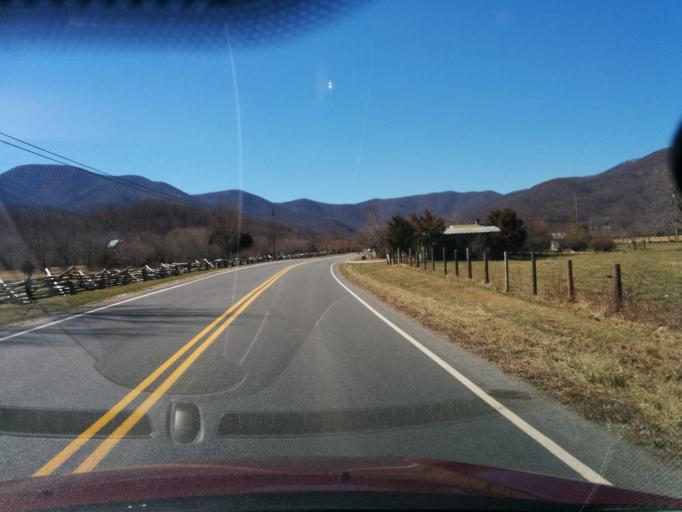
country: US
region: Virginia
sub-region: Nelson County
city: Nellysford
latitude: 37.8724
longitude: -78.9215
